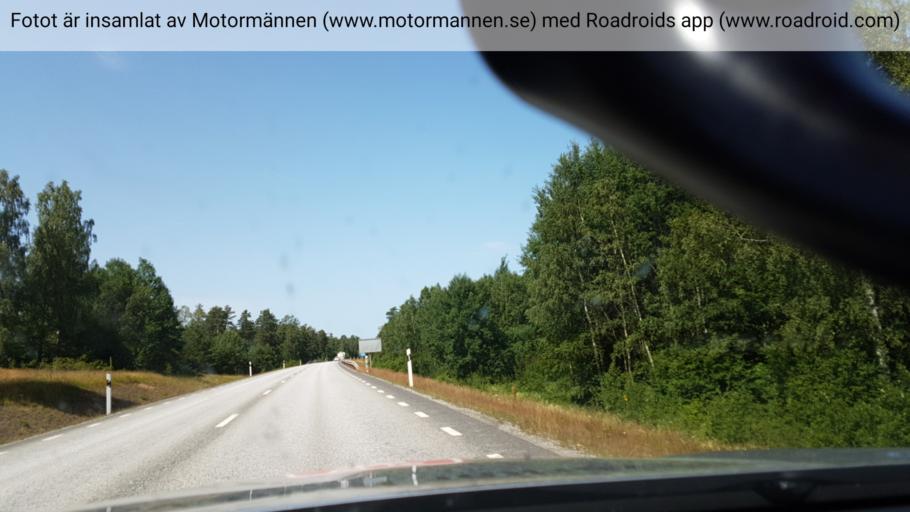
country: SE
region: Joenkoeping
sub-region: Eksjo Kommun
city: Eksjoe
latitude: 57.6671
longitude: 14.9541
